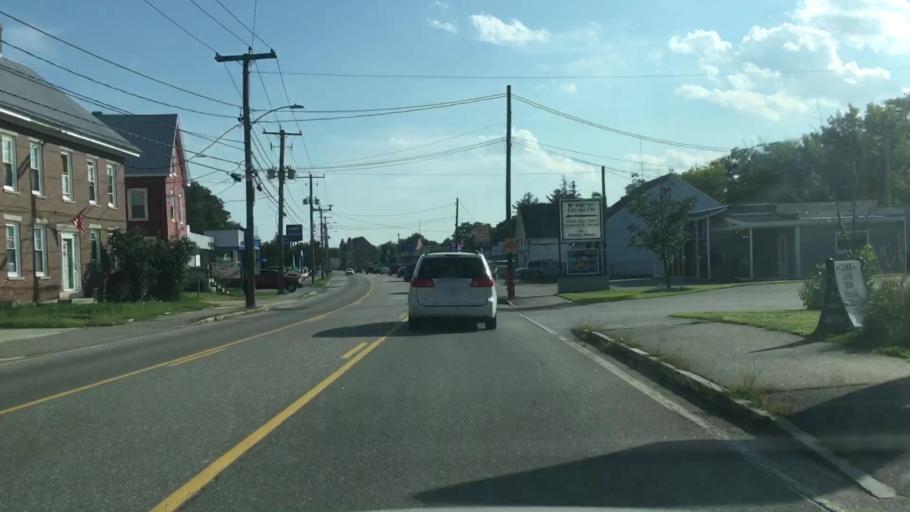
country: US
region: New Hampshire
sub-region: Belknap County
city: Laconia
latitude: 43.5445
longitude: -71.4647
